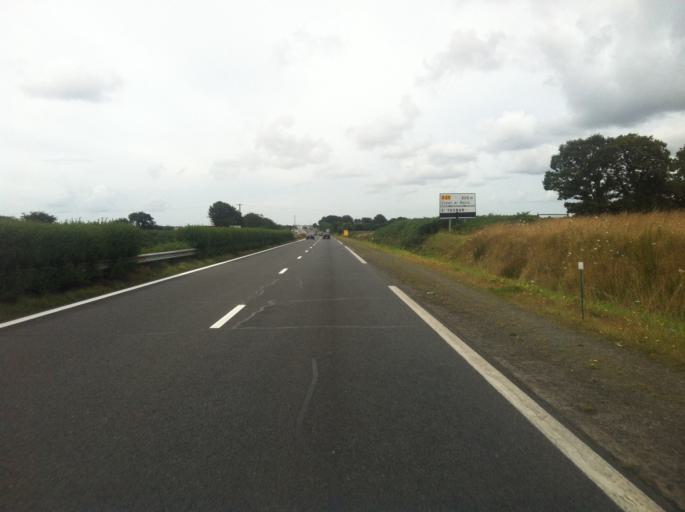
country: FR
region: Brittany
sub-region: Departement du Finistere
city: Saint-Thonan
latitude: 48.4771
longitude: -4.3140
